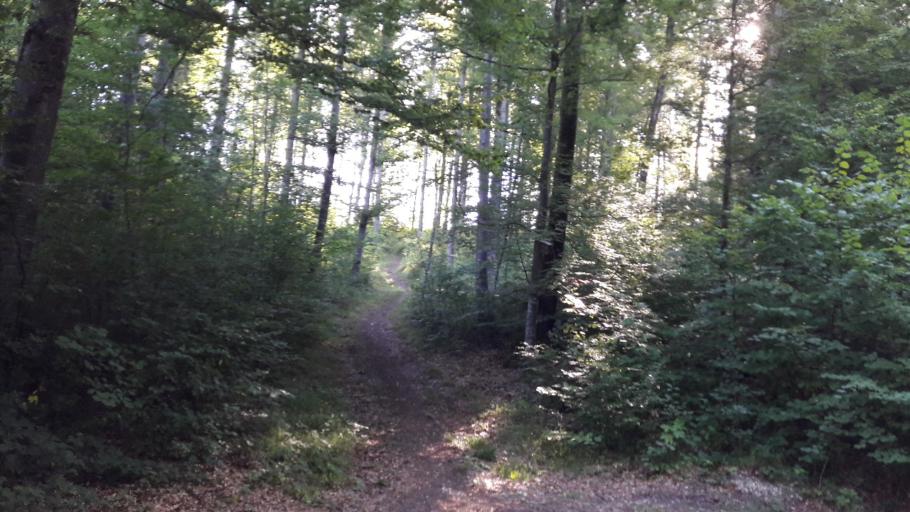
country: CH
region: Solothurn
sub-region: Bezirk Thal
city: Laupersdorf
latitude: 47.3203
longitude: 7.6632
